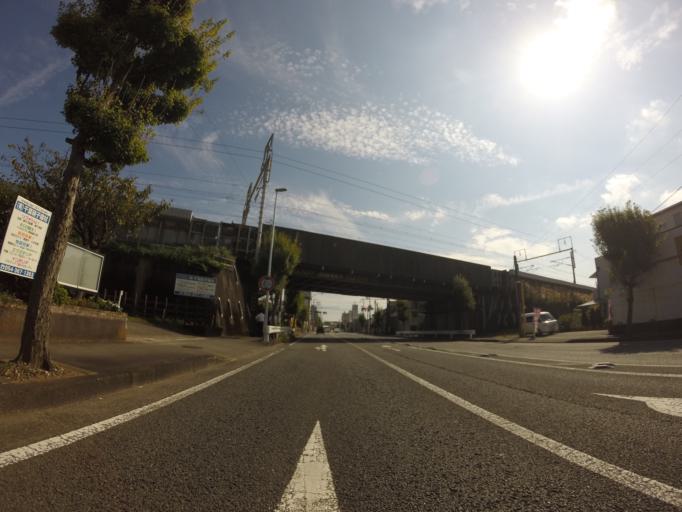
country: JP
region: Shizuoka
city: Shizuoka-shi
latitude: 35.0312
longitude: 138.4781
